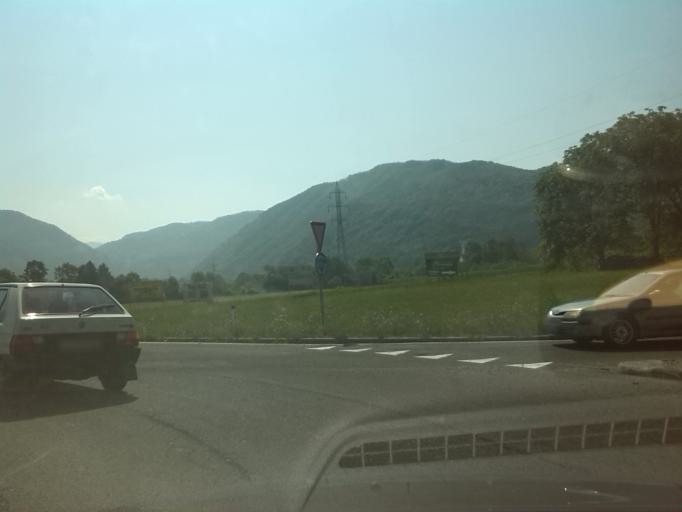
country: SI
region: Tolmin
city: Tolmin
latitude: 46.1828
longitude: 13.7125
